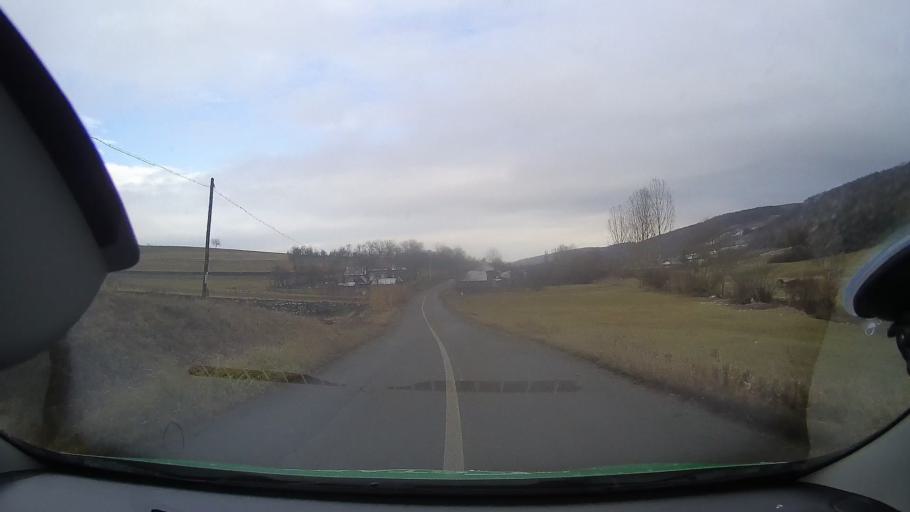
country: RO
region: Alba
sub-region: Comuna Farau
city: Farau
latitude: 46.3897
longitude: 24.0312
